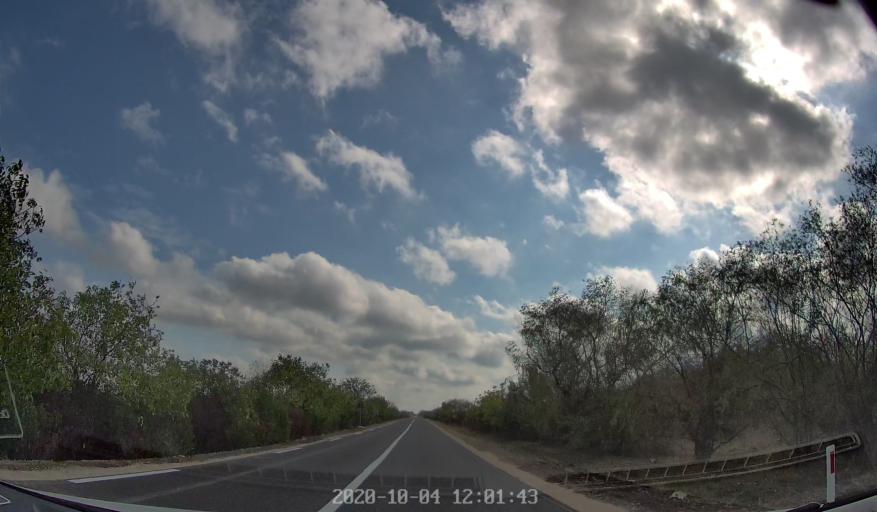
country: MD
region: Rezina
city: Saharna
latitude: 47.6226
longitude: 28.8937
